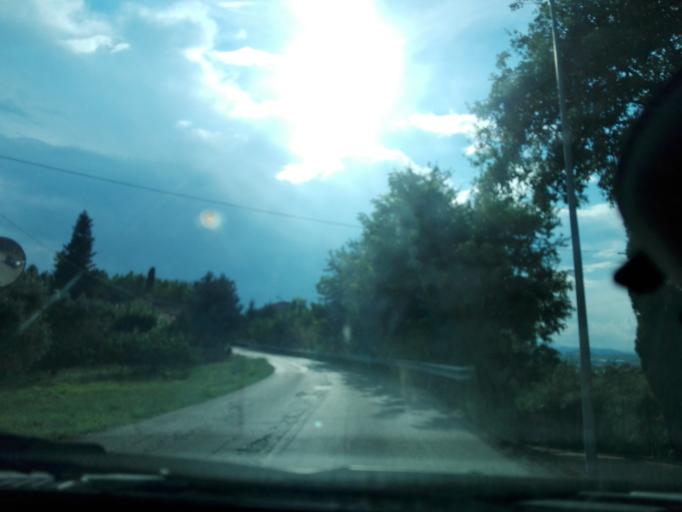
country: IT
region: Abruzzo
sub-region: Provincia di Pescara
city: Cappelle sul Tavo
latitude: 42.4559
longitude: 14.0941
